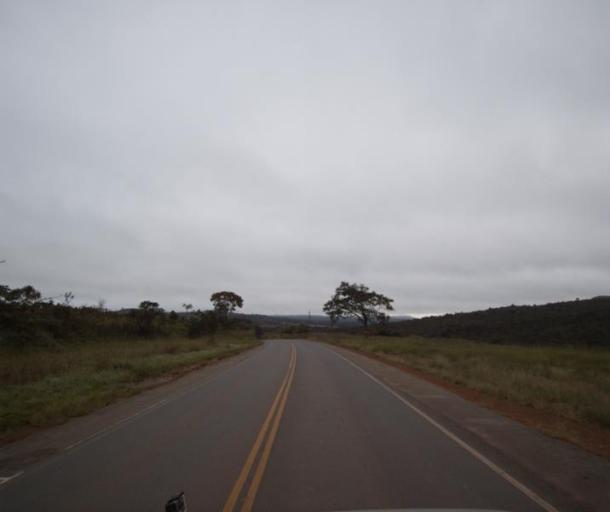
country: BR
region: Goias
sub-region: Pirenopolis
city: Pirenopolis
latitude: -15.8951
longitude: -48.7960
